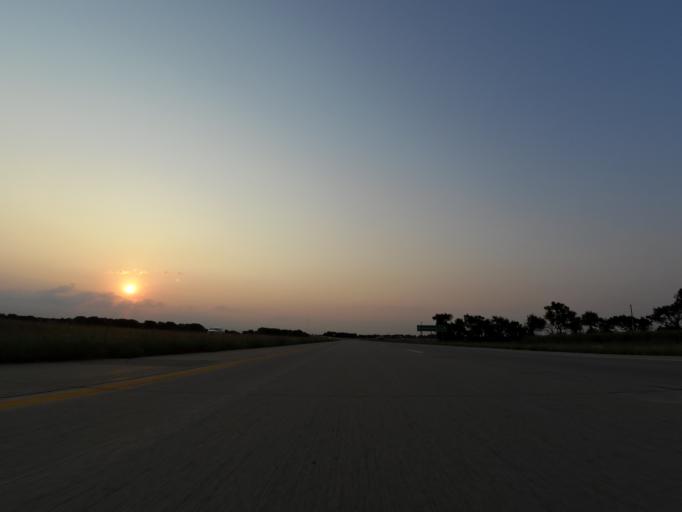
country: US
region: Kansas
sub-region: Reno County
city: Haven
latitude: 37.8773
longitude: -97.7045
